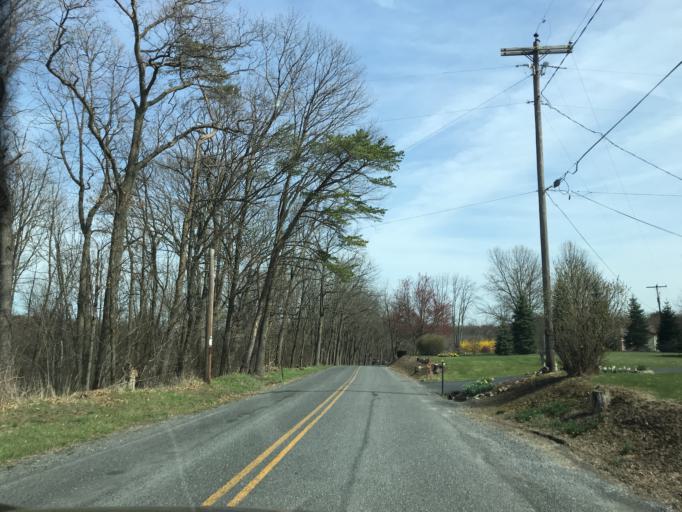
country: US
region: Pennsylvania
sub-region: Northumberland County
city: Northumberland
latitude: 40.8814
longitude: -76.8130
